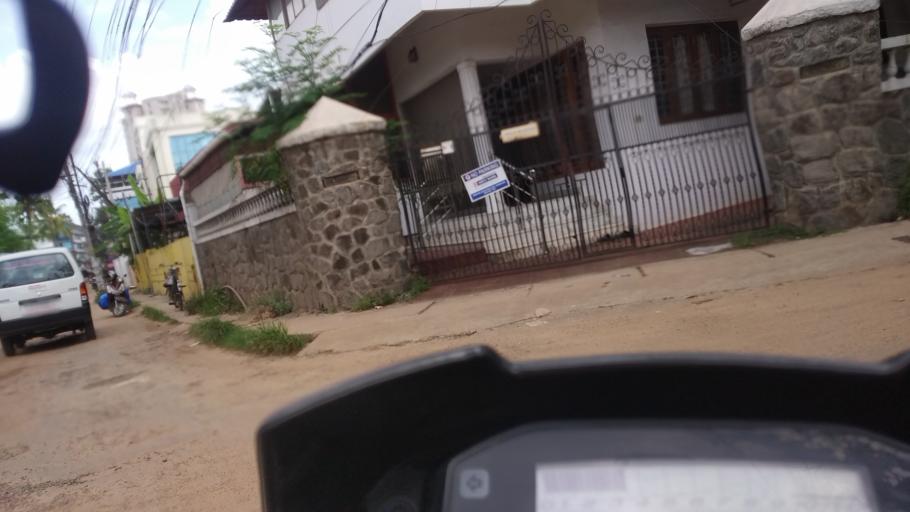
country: IN
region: Kerala
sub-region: Ernakulam
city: Cochin
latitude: 9.9854
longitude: 76.2950
